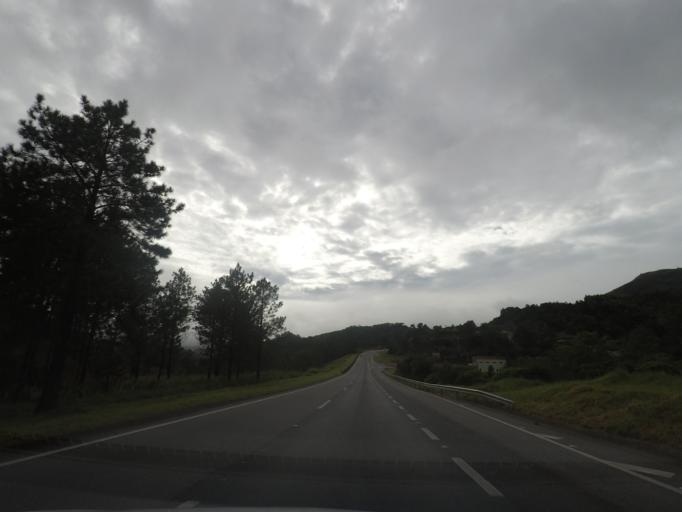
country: BR
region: Parana
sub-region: Campina Grande Do Sul
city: Campina Grande do Sul
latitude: -25.1090
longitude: -48.8372
